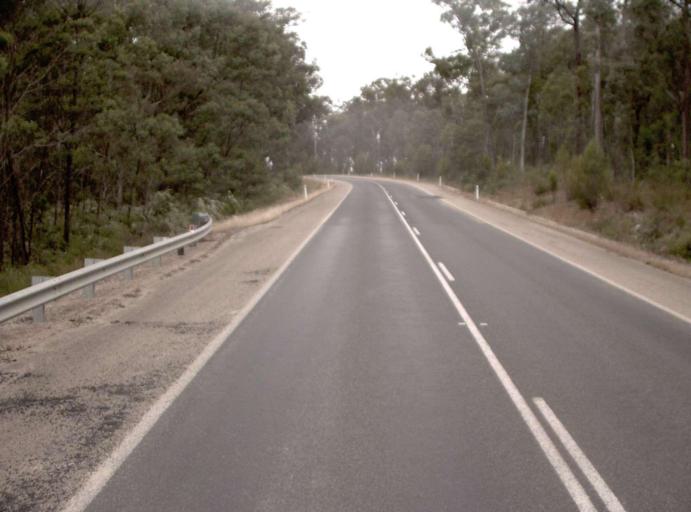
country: AU
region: Victoria
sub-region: East Gippsland
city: Lakes Entrance
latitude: -37.7242
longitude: 147.8824
